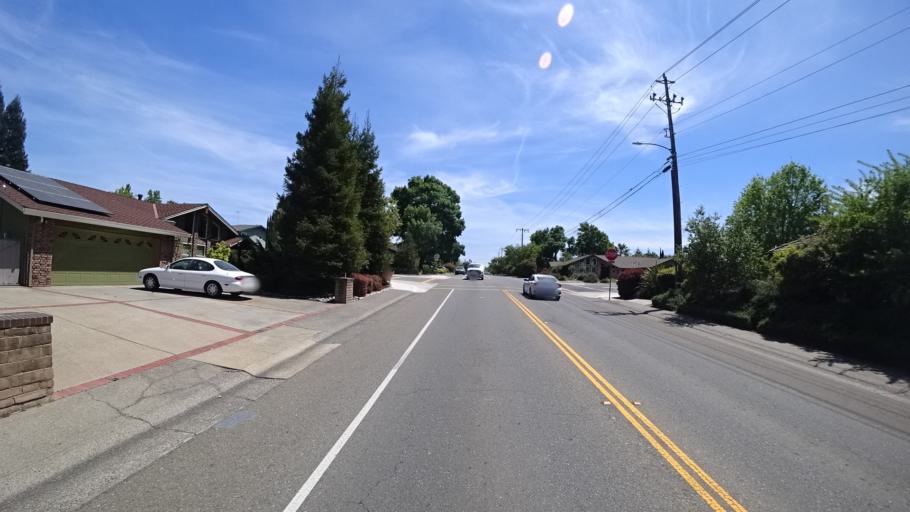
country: US
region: California
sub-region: Placer County
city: Rocklin
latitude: 38.7981
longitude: -121.2379
